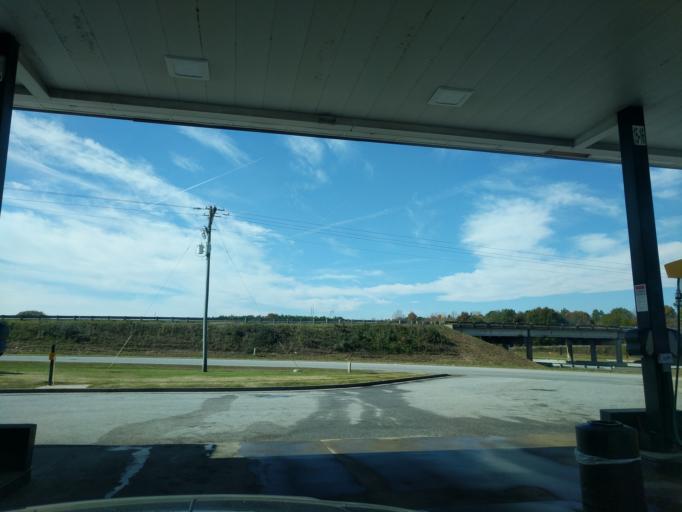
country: US
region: South Carolina
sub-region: Cherokee County
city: Blacksburg
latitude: 35.1568
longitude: -81.4788
